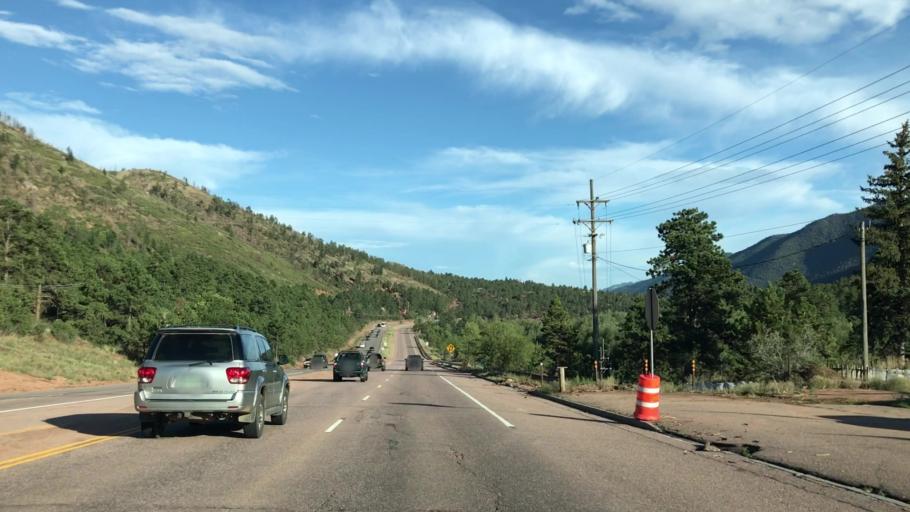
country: US
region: Colorado
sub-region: El Paso County
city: Cascade-Chipita Park
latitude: 38.9120
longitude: -104.9768
